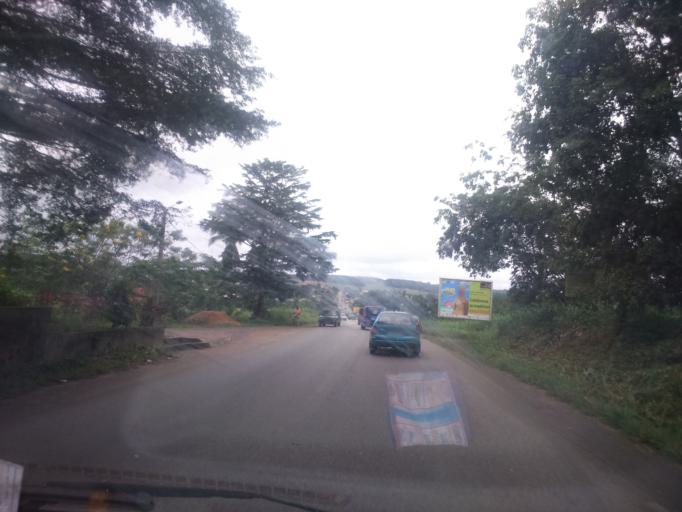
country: CI
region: Sud-Comoe
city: Bonoua
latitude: 5.2810
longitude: -3.5235
